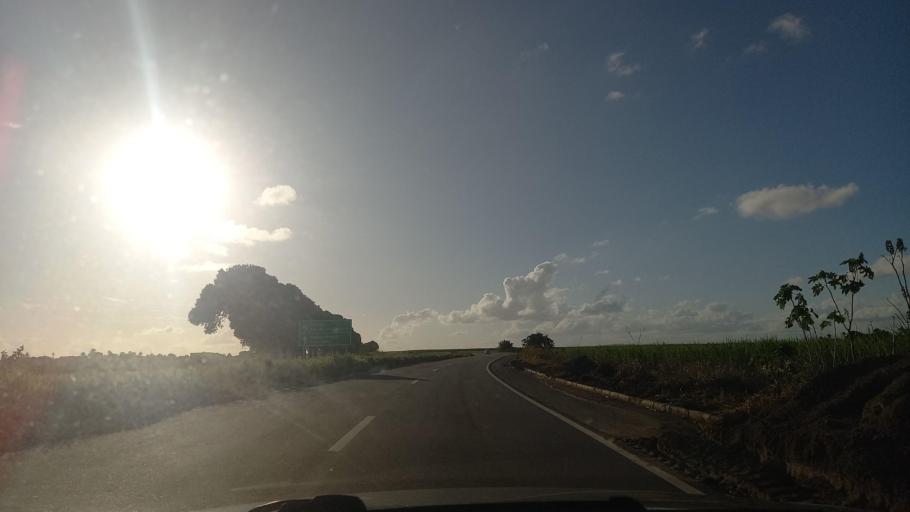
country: BR
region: Alagoas
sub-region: Campo Alegre
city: Campo Alegre
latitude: -9.8092
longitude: -36.2589
